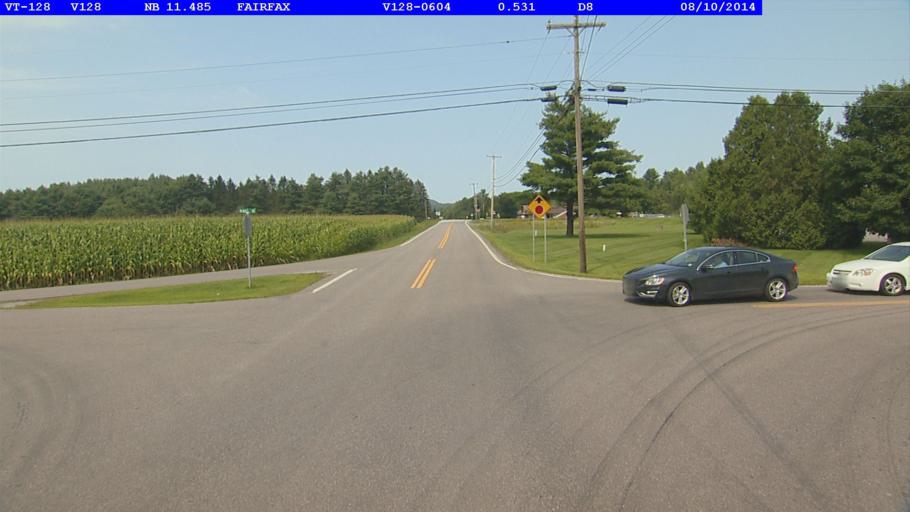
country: US
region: Vermont
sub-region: Chittenden County
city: Milton
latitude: 44.6541
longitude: -73.0098
